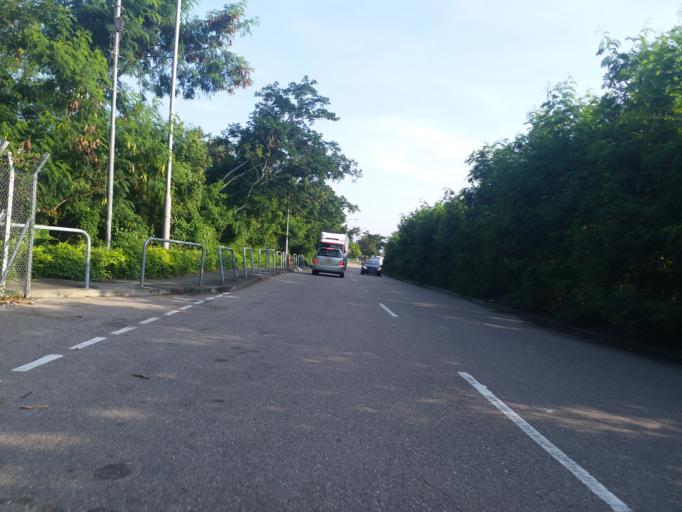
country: HK
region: Yuen Long
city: Yuen Long Kau Hui
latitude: 22.4749
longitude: 114.0516
